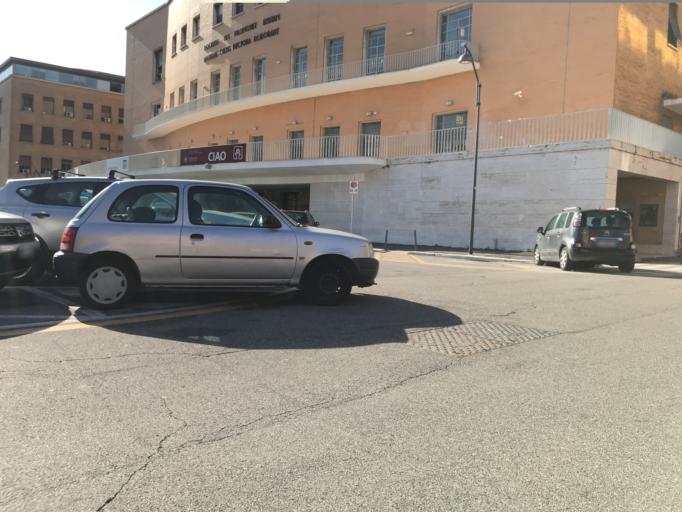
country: IT
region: Latium
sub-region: Citta metropolitana di Roma Capitale
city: Rome
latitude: 41.9036
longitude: 12.5159
